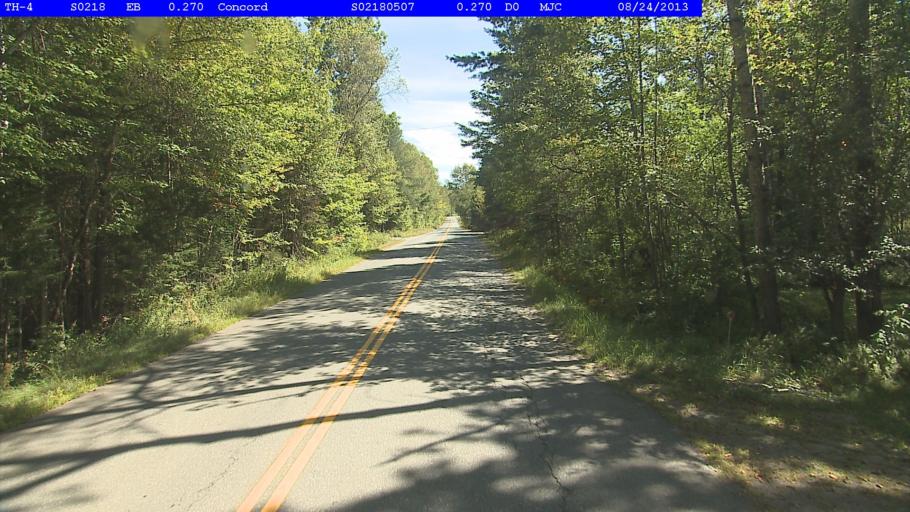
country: US
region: New Hampshire
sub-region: Grafton County
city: Littleton
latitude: 44.4613
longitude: -71.7730
